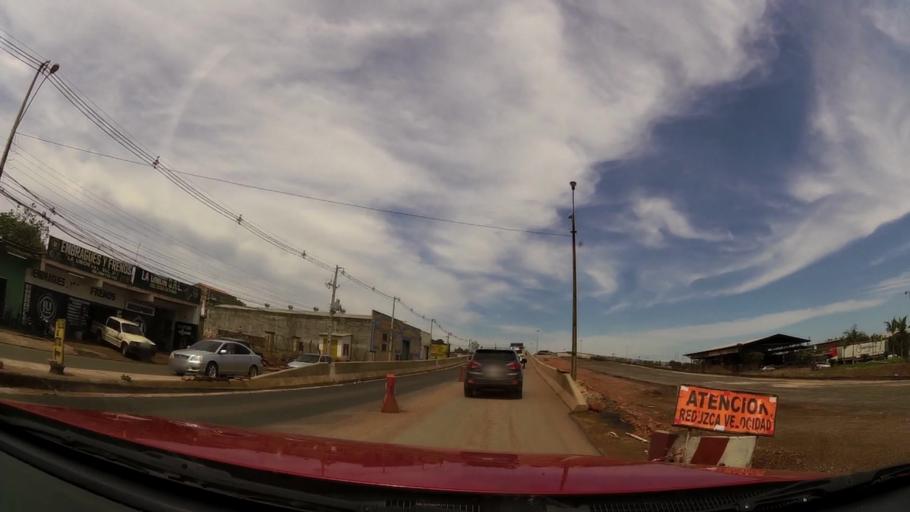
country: PY
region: Central
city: Colonia Mariano Roque Alonso
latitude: -25.2018
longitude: -57.5225
